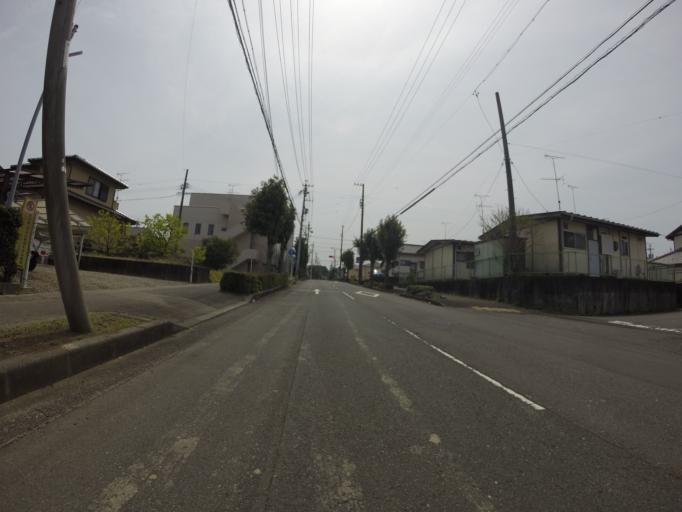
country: JP
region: Shizuoka
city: Kakegawa
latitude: 34.7659
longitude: 138.0057
